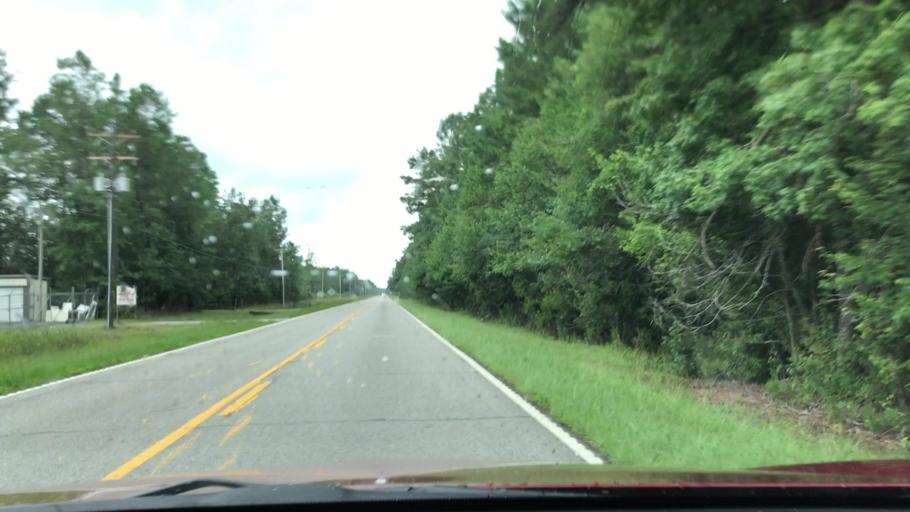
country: US
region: South Carolina
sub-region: Georgetown County
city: Georgetown
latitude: 33.5234
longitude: -79.2442
